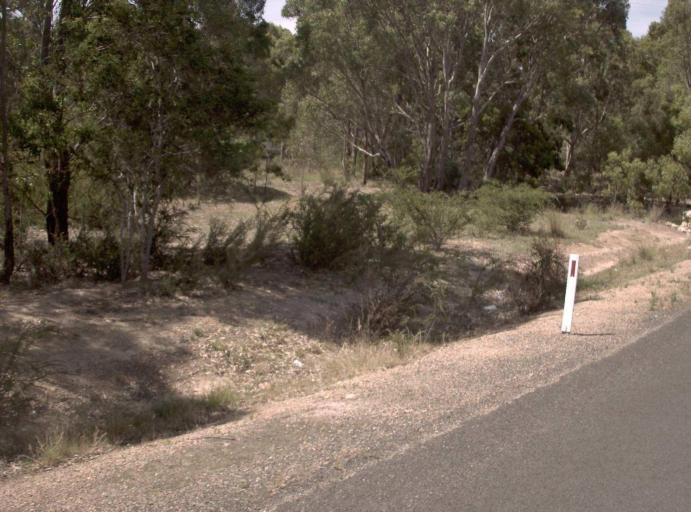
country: AU
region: Victoria
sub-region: Wellington
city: Sale
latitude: -37.9607
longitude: 147.0940
